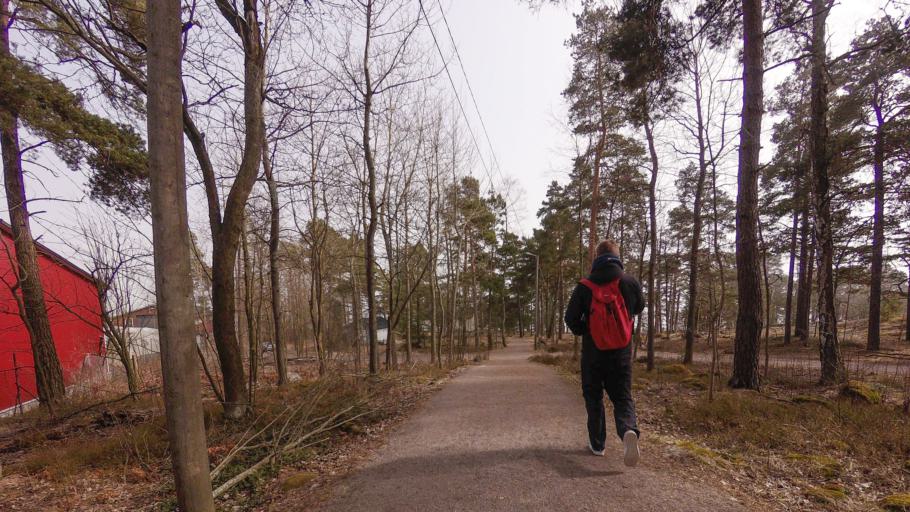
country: FI
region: Uusimaa
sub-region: Helsinki
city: Helsinki
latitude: 60.1812
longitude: 24.9981
